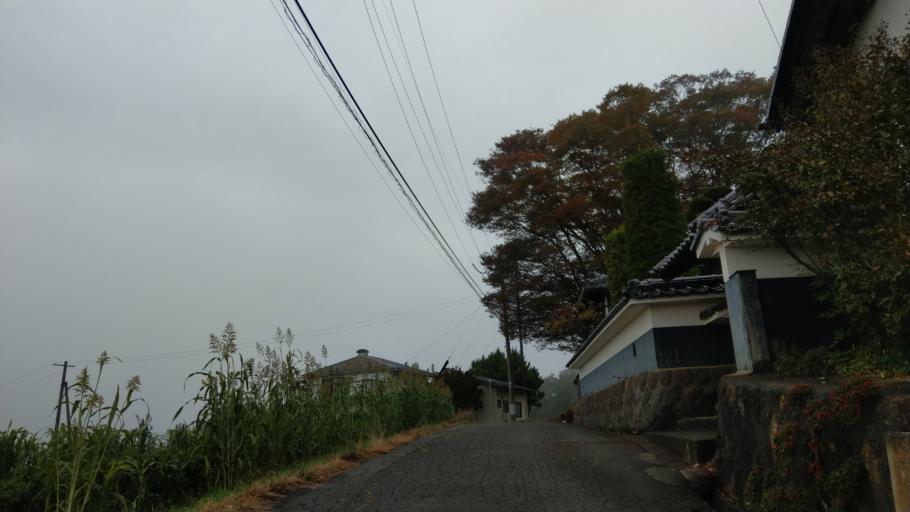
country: JP
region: Nagano
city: Komoro
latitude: 36.3569
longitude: 138.4229
